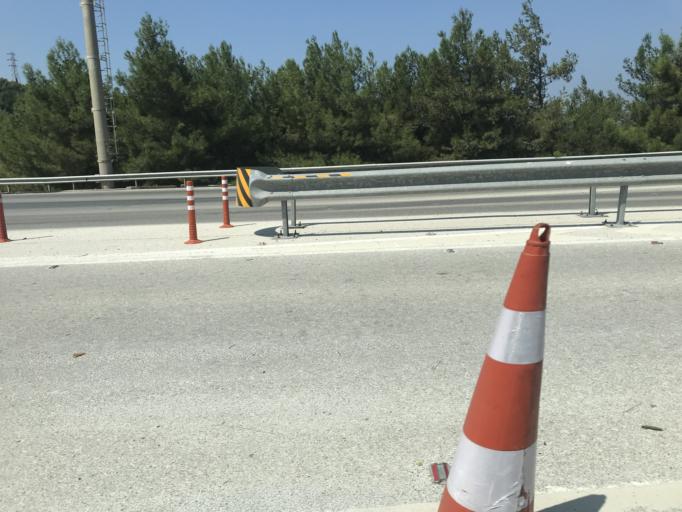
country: TR
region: Izmir
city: Urla
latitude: 38.3228
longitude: 26.7821
